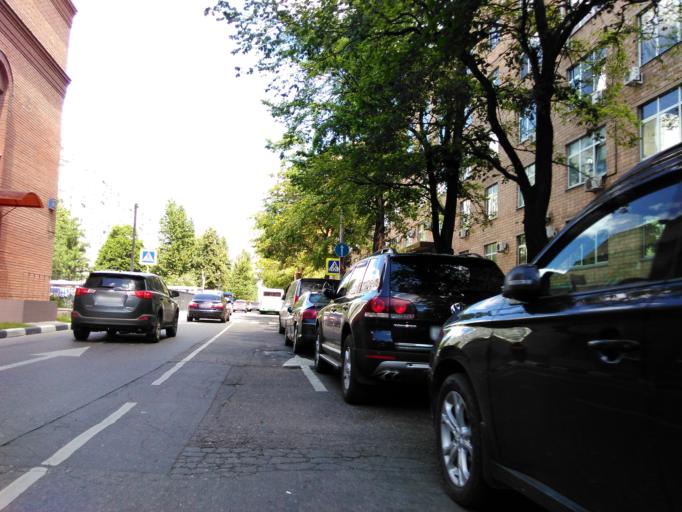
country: RU
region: Moskovskaya
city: Cheremushki
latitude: 55.6683
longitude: 37.5651
